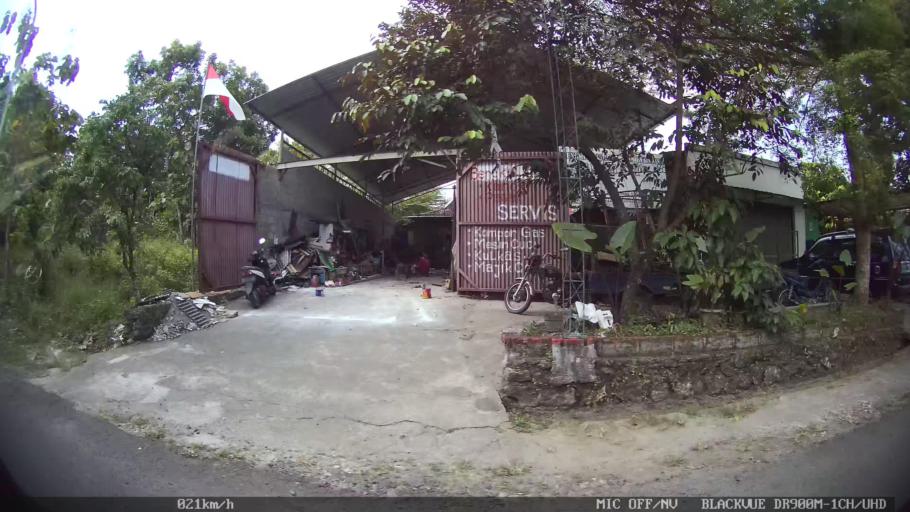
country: ID
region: Daerah Istimewa Yogyakarta
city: Bantul
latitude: -7.8623
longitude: 110.3072
